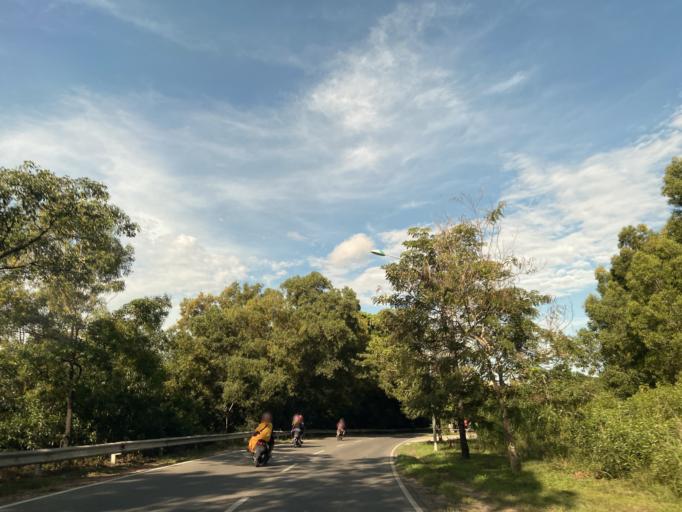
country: SG
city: Singapore
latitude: 1.1233
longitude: 104.0099
